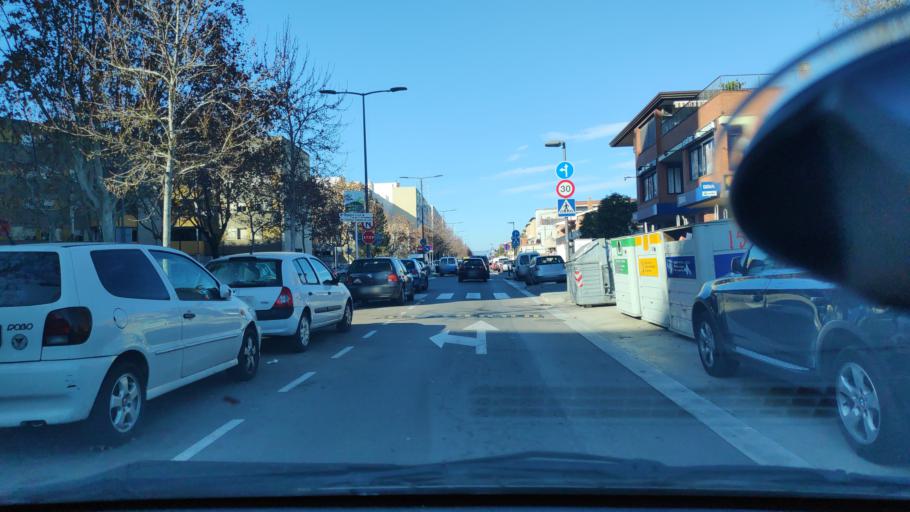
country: ES
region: Catalonia
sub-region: Provincia de Barcelona
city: Barbera del Valles
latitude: 41.5084
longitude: 2.1190
